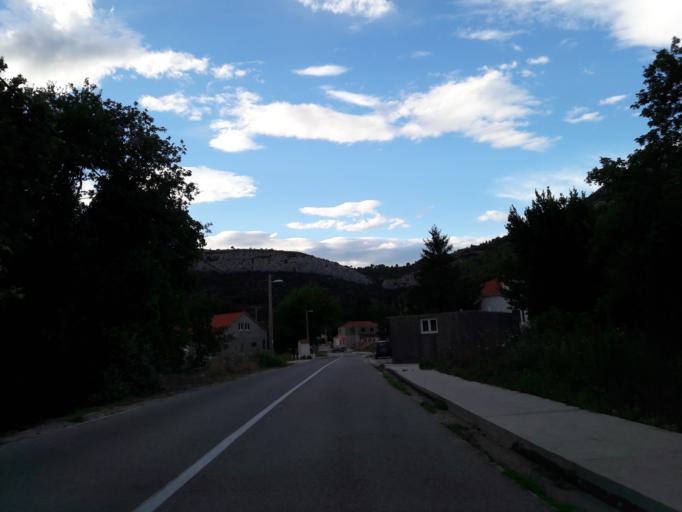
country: HR
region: Dubrovacko-Neretvanska
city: Ston
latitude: 42.8433
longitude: 17.6312
